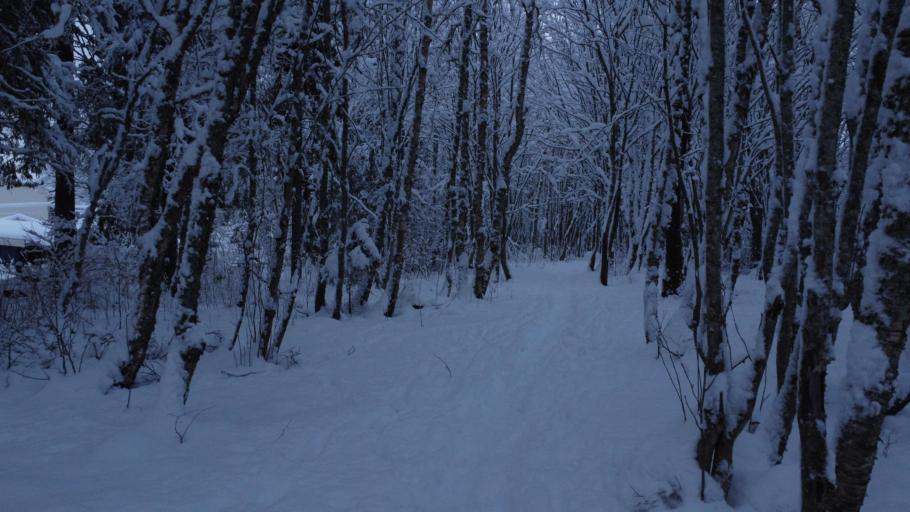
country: NO
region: Nordland
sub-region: Rana
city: Mo i Rana
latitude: 66.3356
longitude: 14.1496
